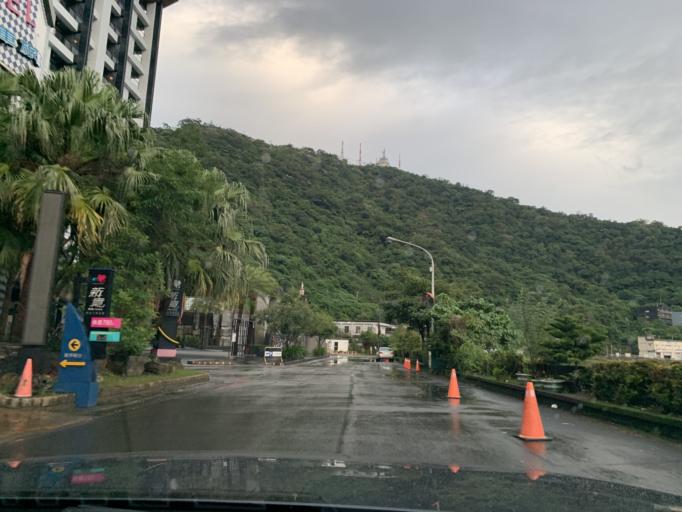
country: TW
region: Taiwan
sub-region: Yilan
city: Yilan
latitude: 24.5976
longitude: 121.8534
